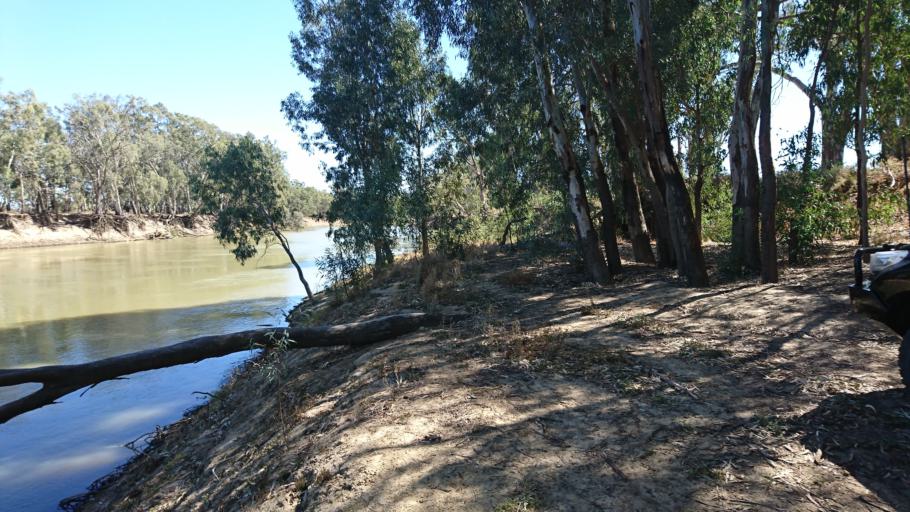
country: AU
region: Victoria
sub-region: Swan Hill
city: Swan Hill
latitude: -35.0028
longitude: 143.3364
